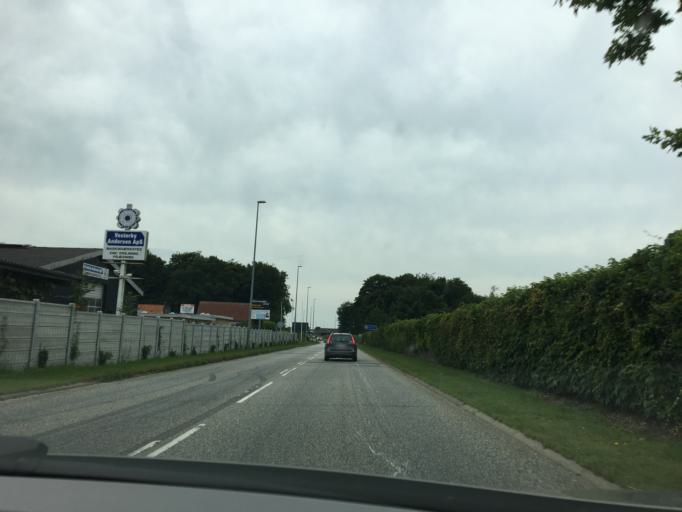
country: DK
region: Central Jutland
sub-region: Herning Kommune
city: Herning
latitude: 56.1344
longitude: 8.9455
